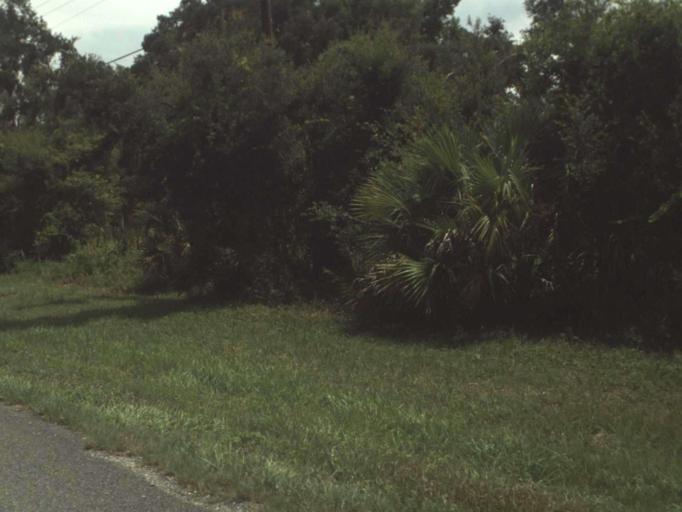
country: US
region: Florida
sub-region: Sumter County
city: Lake Panasoffkee
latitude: 28.7910
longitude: -82.0701
